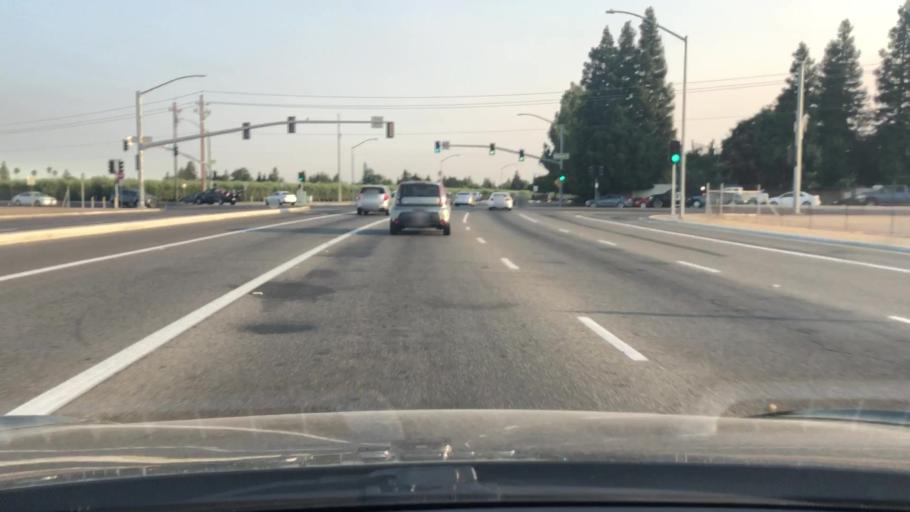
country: US
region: California
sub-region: Fresno County
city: Clovis
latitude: 36.8225
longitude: -119.7288
